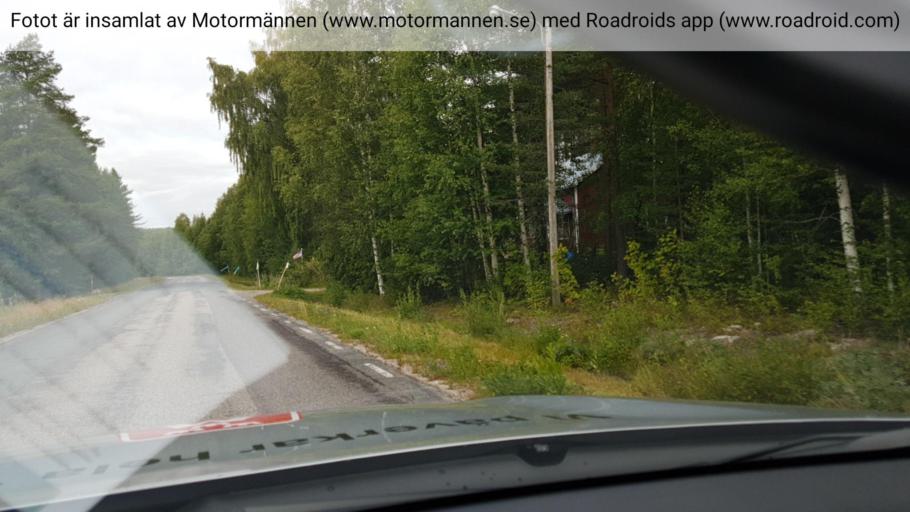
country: SE
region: Norrbotten
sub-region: Bodens Kommun
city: Saevast
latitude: 65.6684
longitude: 21.7407
